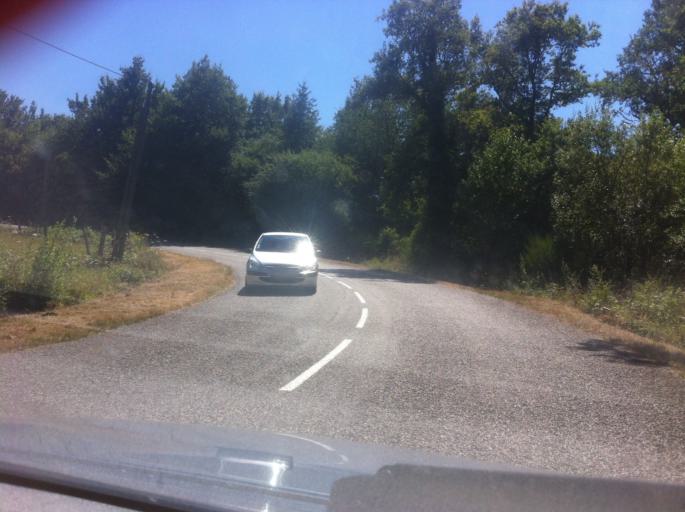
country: FR
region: Auvergne
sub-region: Departement de l'Allier
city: Montmarault
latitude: 46.3072
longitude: 3.0246
